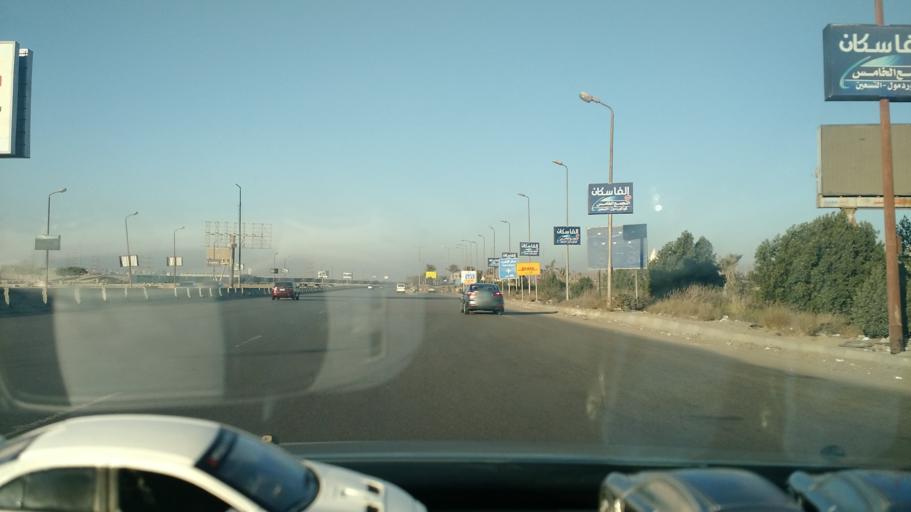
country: EG
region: Muhafazat al Qalyubiyah
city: Al Khankah
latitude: 30.0791
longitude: 31.4276
